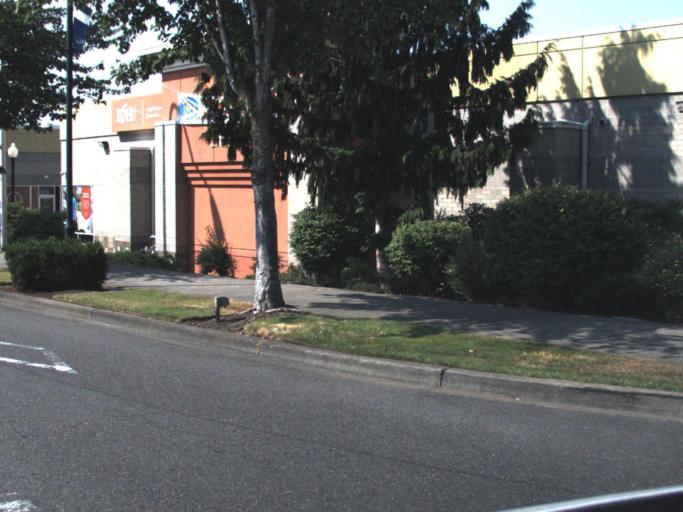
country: US
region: Washington
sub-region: King County
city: Federal Way
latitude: 47.3204
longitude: -122.3135
